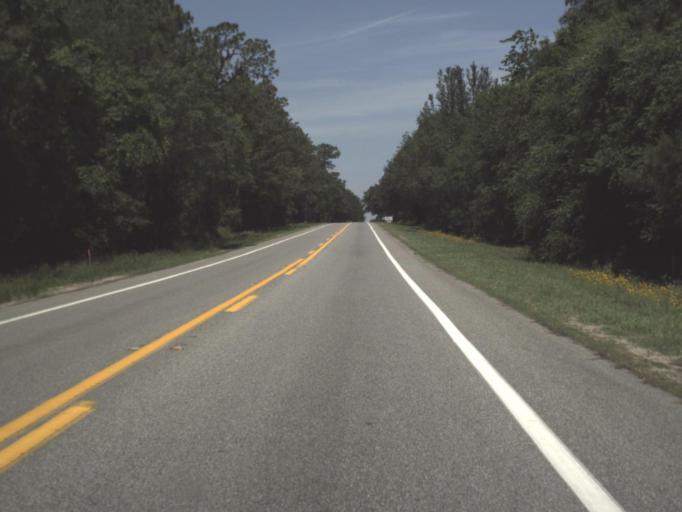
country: US
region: Florida
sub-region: Suwannee County
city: Live Oak
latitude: 30.3497
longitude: -83.1042
